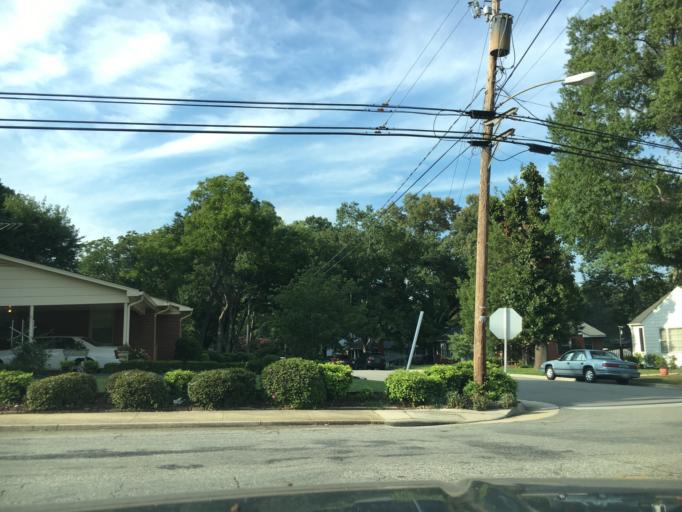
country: US
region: Virginia
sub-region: Halifax County
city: South Boston
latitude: 36.7047
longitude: -78.8954
